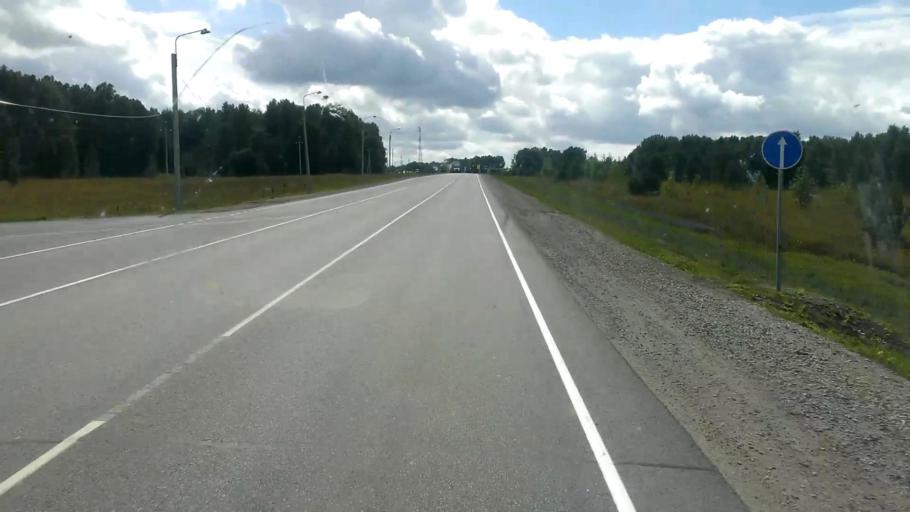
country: RU
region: Altai Krai
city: Troitskoye
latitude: 52.9740
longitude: 84.7473
